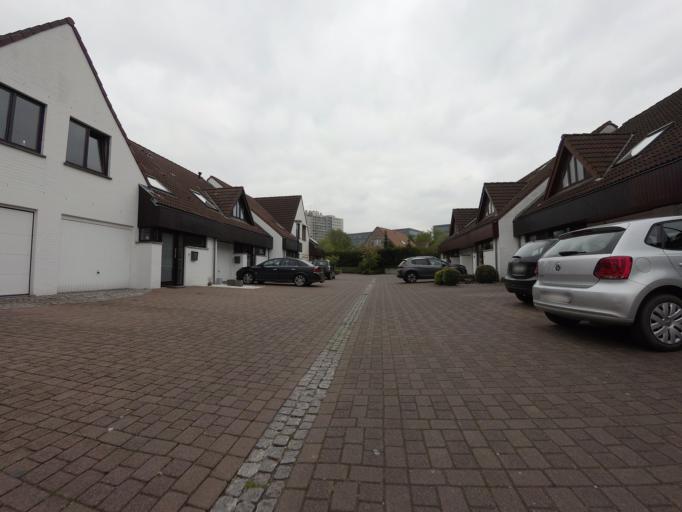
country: BE
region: Flanders
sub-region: Provincie Vlaams-Brabant
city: Grimbergen
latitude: 50.9168
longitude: 4.3980
